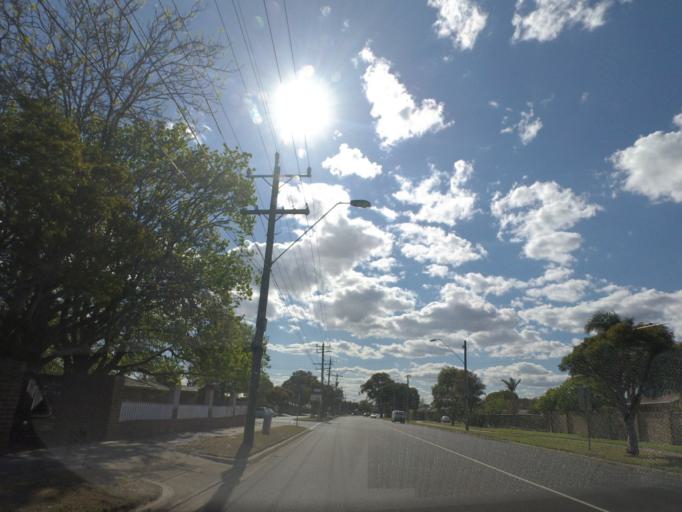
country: AU
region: Victoria
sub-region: Kingston
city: Dingley Village
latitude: -37.9818
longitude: 145.1296
